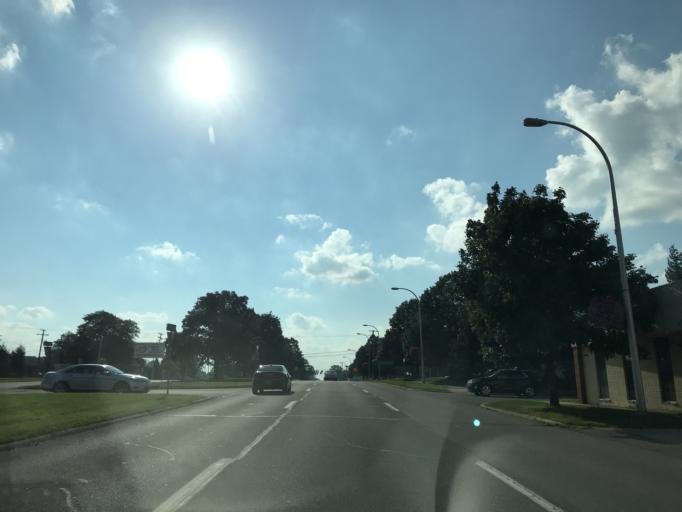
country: US
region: Michigan
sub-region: Wayne County
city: Livonia
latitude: 42.3973
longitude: -83.3702
